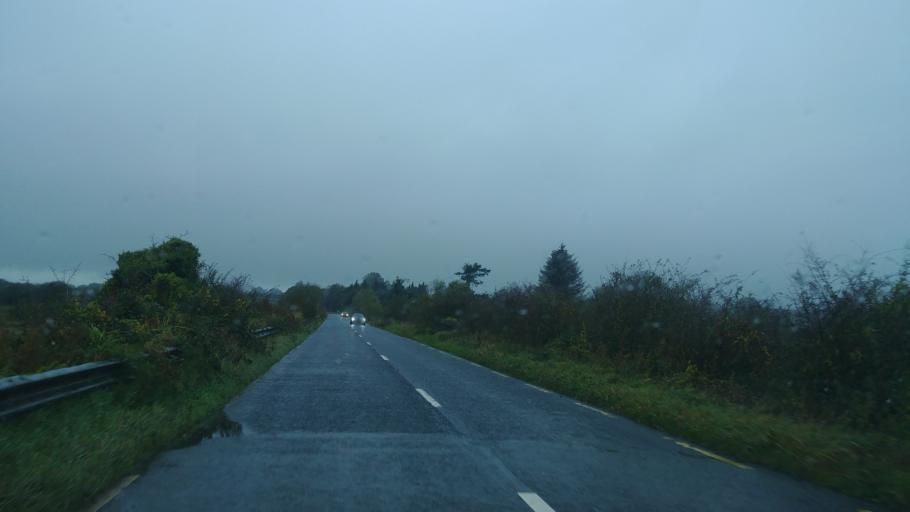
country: IE
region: Connaught
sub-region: Roscommon
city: Ballaghaderreen
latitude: 53.9082
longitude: -8.5927
